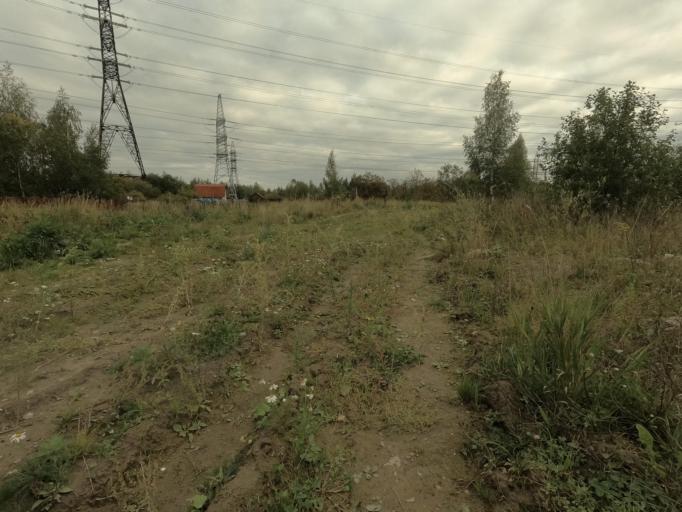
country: RU
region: St.-Petersburg
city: Metallostroy
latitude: 59.8148
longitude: 30.5466
